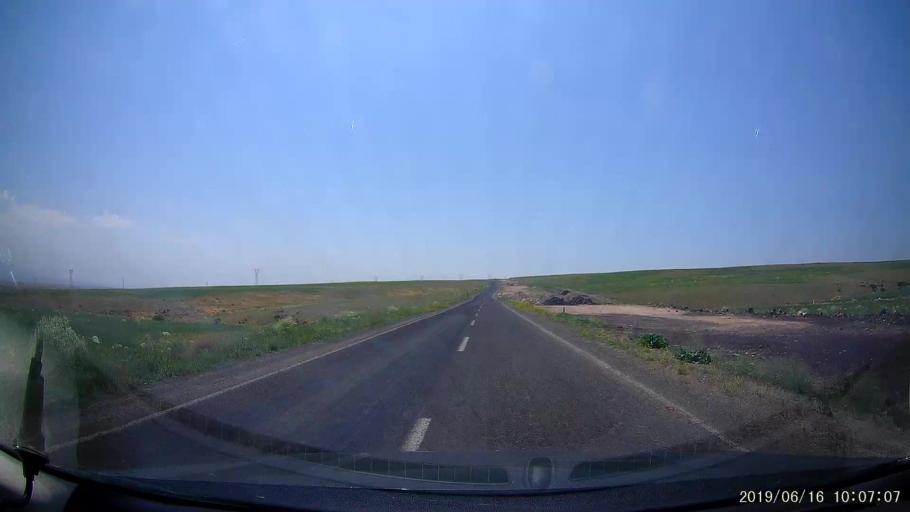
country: TR
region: Kars
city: Digor
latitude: 40.2477
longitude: 43.5515
